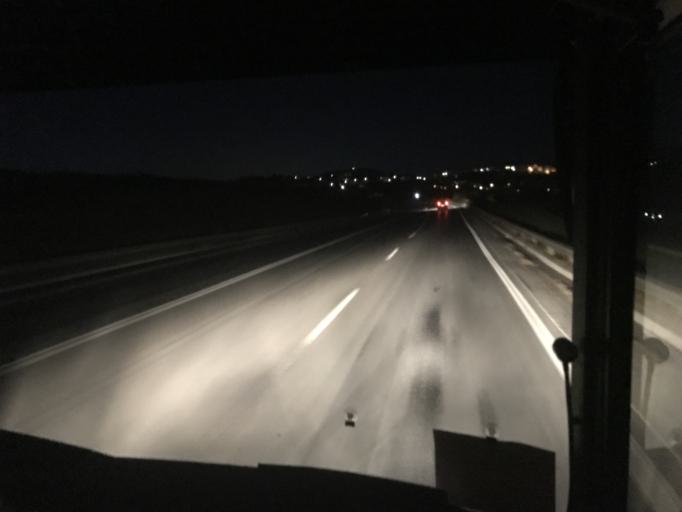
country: GR
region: Crete
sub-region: Nomos Irakleiou
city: Skalanion
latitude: 35.2704
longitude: 25.1848
